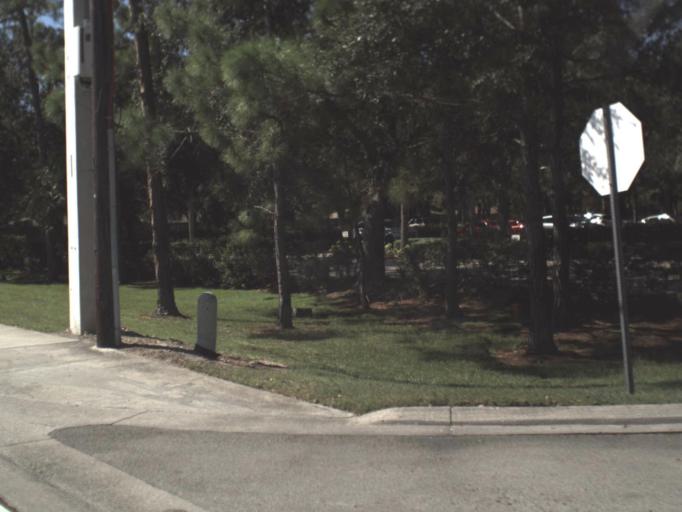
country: US
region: Florida
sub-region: Collier County
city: Pine Ridge
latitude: 26.1908
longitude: -81.7679
